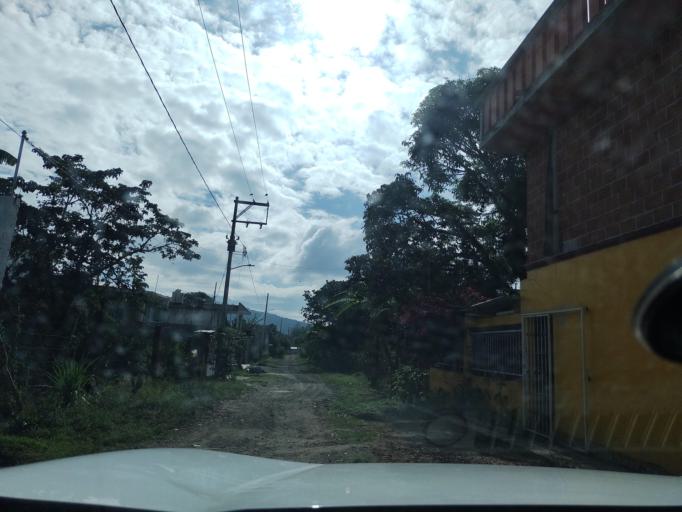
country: MX
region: Veracruz
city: Coatepec
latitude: 19.4807
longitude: -96.9348
